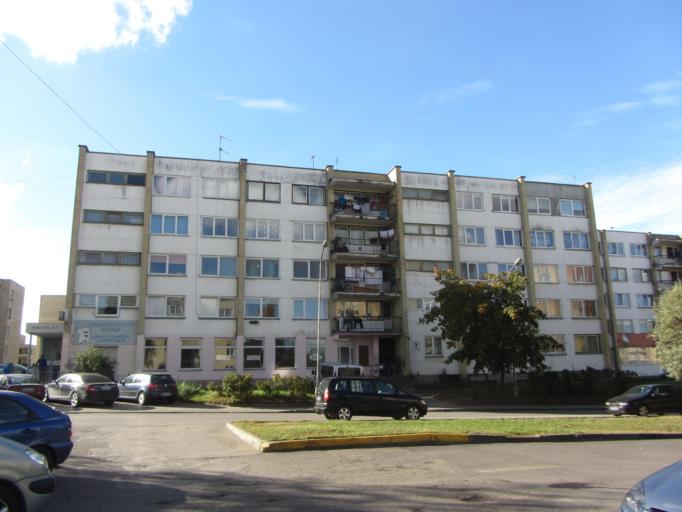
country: LT
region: Utenos apskritis
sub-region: Utena
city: Utena
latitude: 55.5003
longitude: 25.6175
